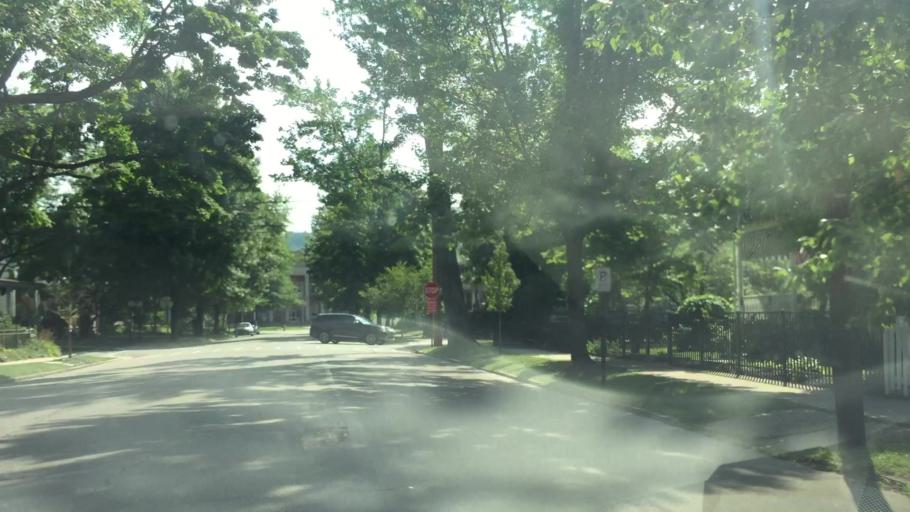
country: US
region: Pennsylvania
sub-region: Allegheny County
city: Sewickley
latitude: 40.5367
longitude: -80.1784
